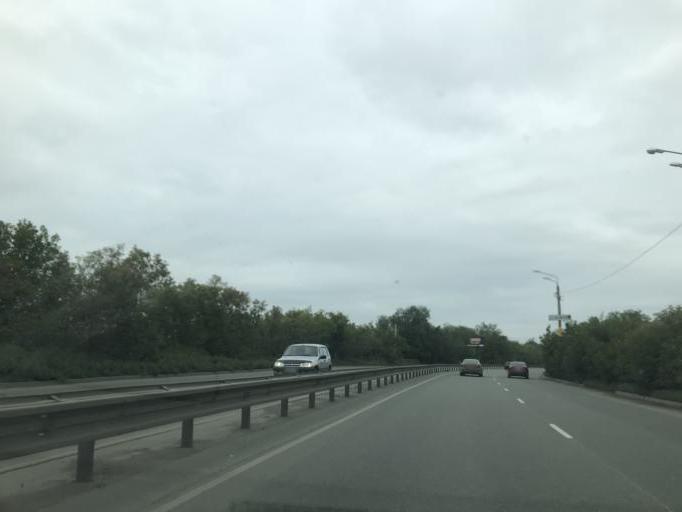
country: RU
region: Chelyabinsk
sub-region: Gorod Chelyabinsk
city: Chelyabinsk
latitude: 55.1742
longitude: 61.4241
